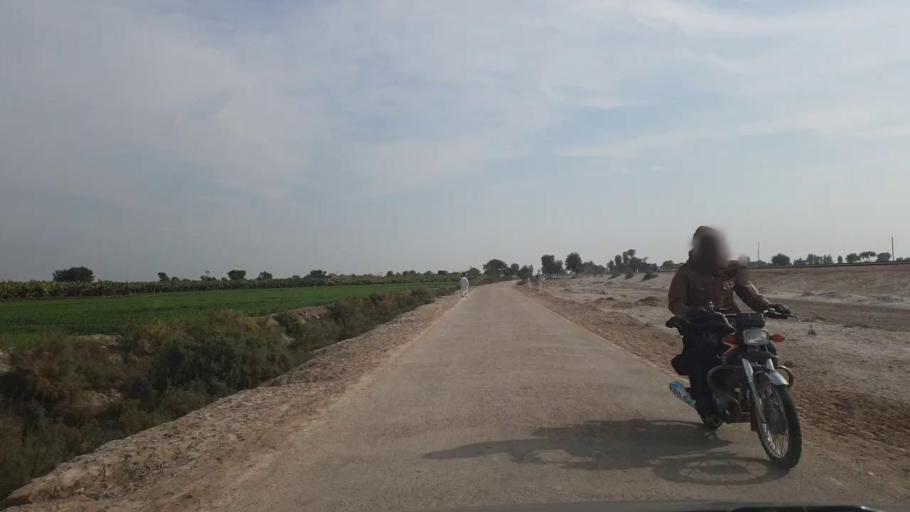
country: PK
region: Sindh
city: Shahpur Chakar
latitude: 26.0856
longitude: 68.4887
